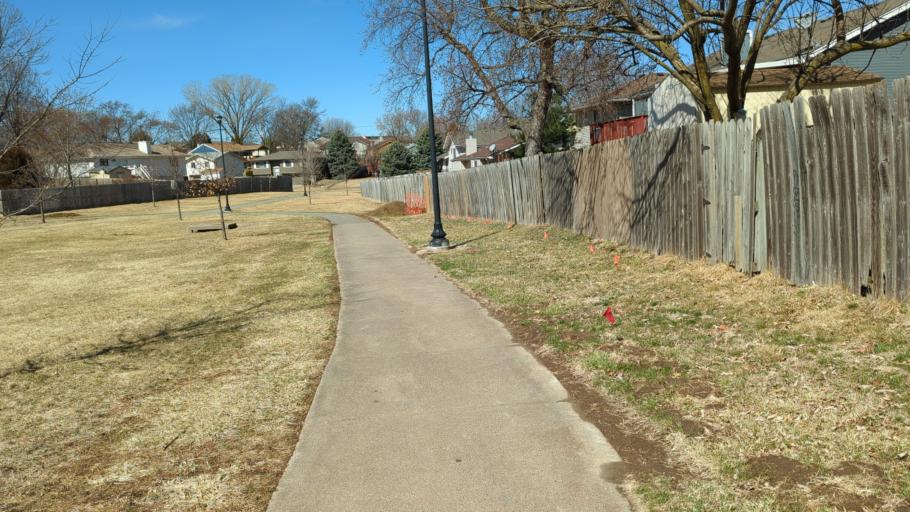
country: US
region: Nebraska
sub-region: Sarpy County
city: Offutt Air Force Base
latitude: 41.1365
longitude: -95.9634
